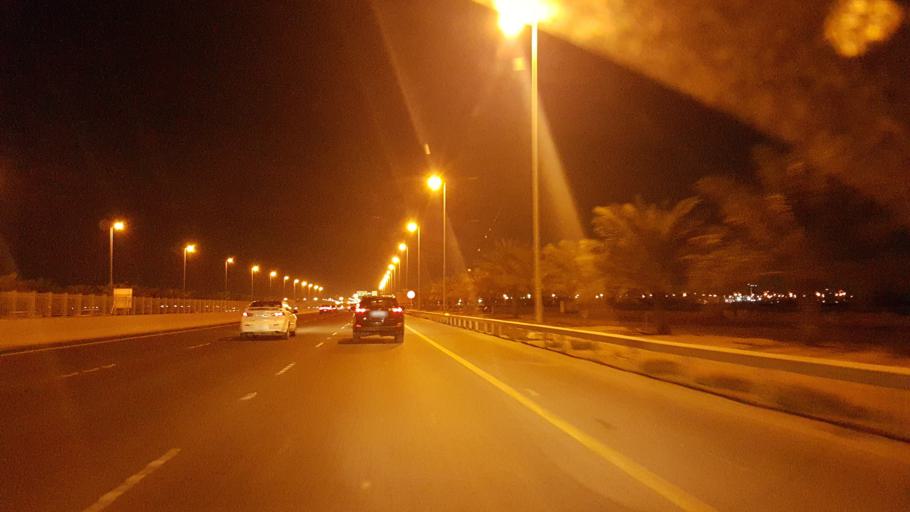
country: BH
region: Muharraq
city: Al Hadd
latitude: 26.2629
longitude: 50.6611
